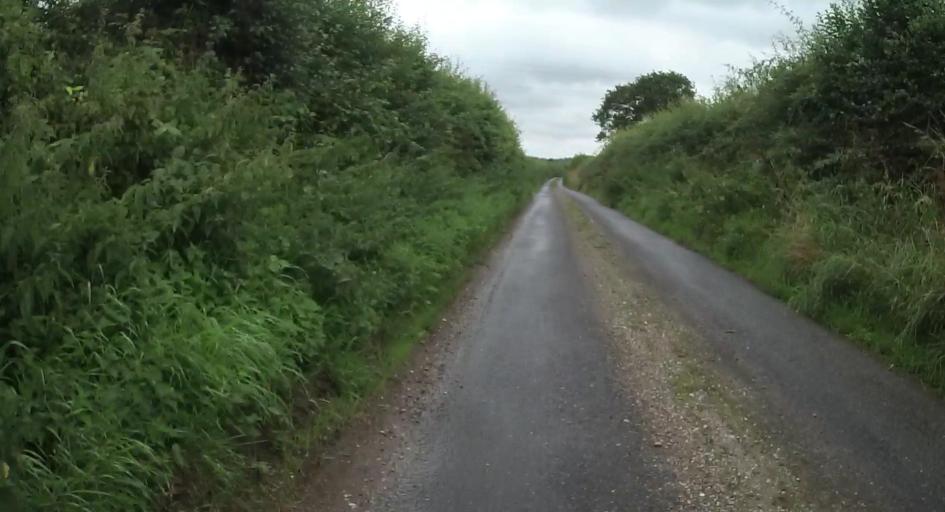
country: GB
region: England
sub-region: Hampshire
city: Andover
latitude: 51.2348
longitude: -1.4154
